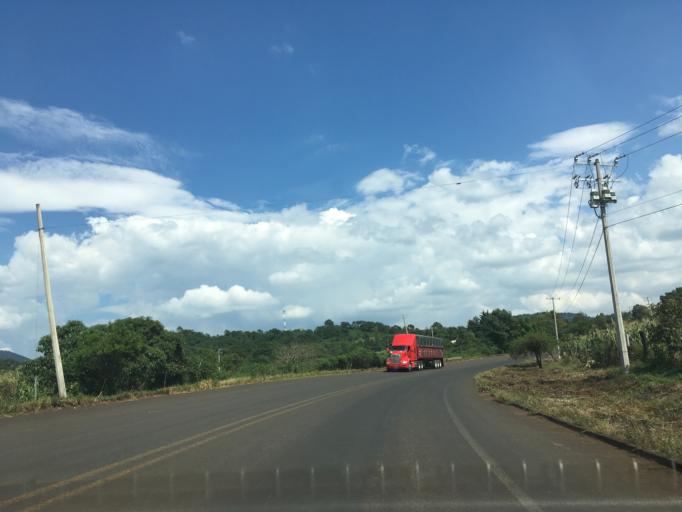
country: MX
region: Michoacan
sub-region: Tingueindin
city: Tingueindin
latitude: 19.8443
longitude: -102.4784
